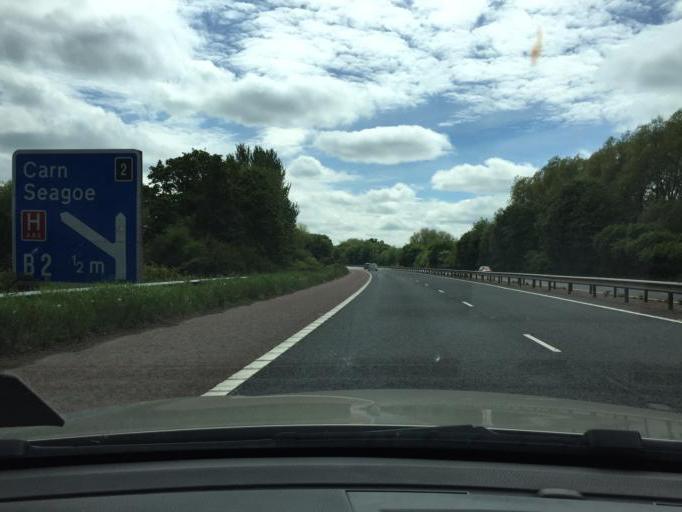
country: GB
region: Northern Ireland
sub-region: Craigavon District
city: Craigavon
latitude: 54.4576
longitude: -6.4244
